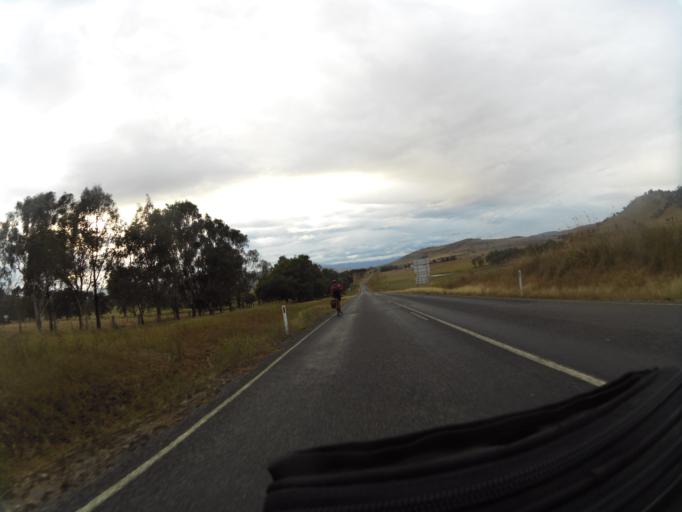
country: AU
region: New South Wales
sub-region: Greater Hume Shire
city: Holbrook
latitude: -36.0523
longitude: 147.9350
